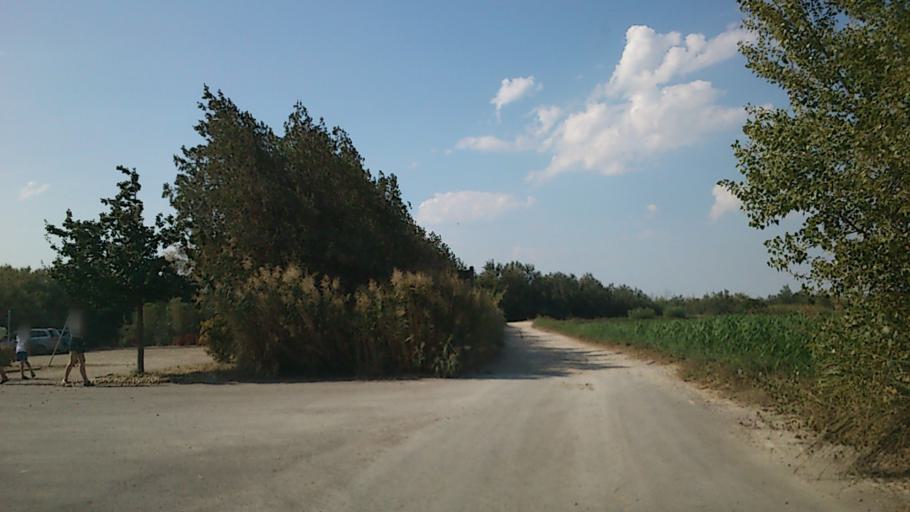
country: ES
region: Aragon
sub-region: Provincia de Zaragoza
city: Puebla de Alfinden
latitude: 41.6080
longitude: -0.7582
